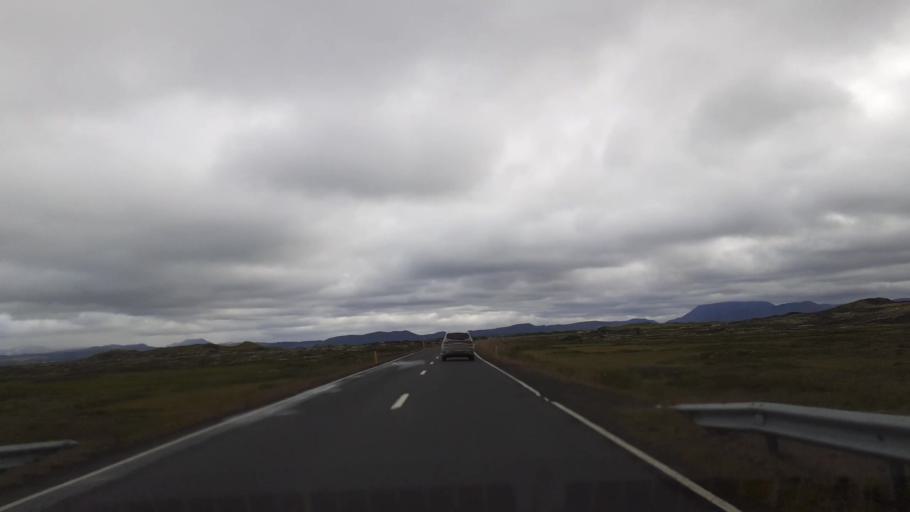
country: IS
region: Northeast
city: Laugar
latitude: 65.5714
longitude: -17.0730
